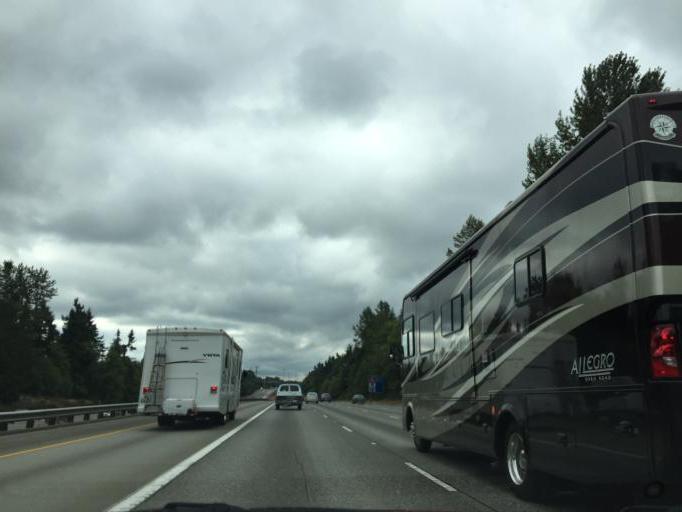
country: US
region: Washington
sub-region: King County
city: Lakeland North
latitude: 47.3332
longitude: -122.2938
